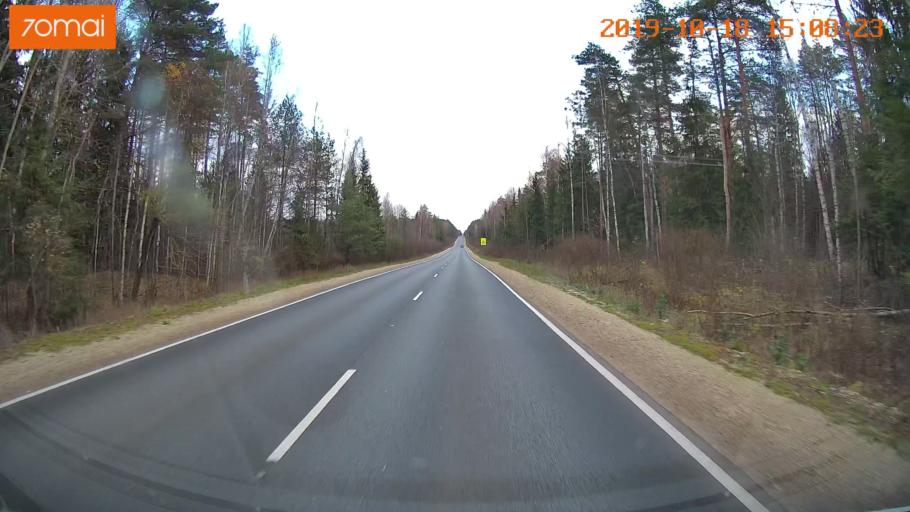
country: RU
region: Vladimir
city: Gus'-Khrustal'nyy
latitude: 55.5516
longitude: 40.6099
